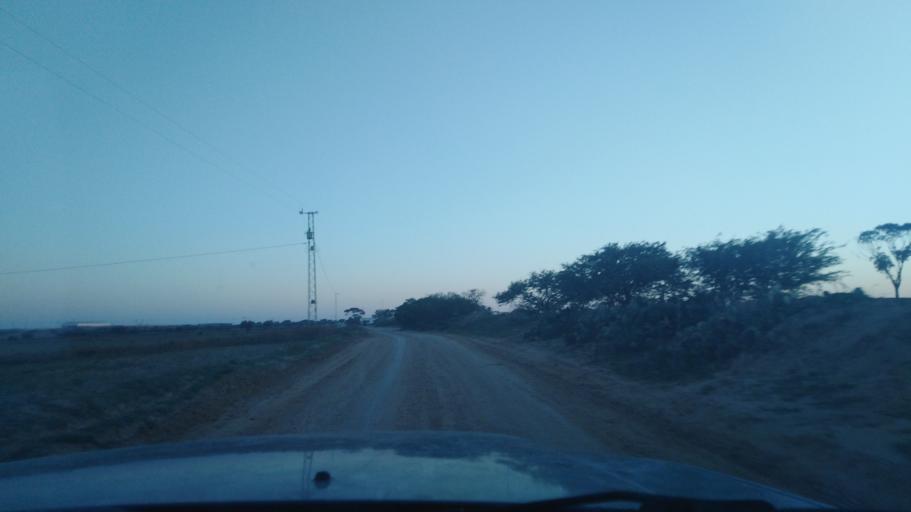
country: TN
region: Safaqis
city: Sfax
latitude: 34.7317
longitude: 10.4452
